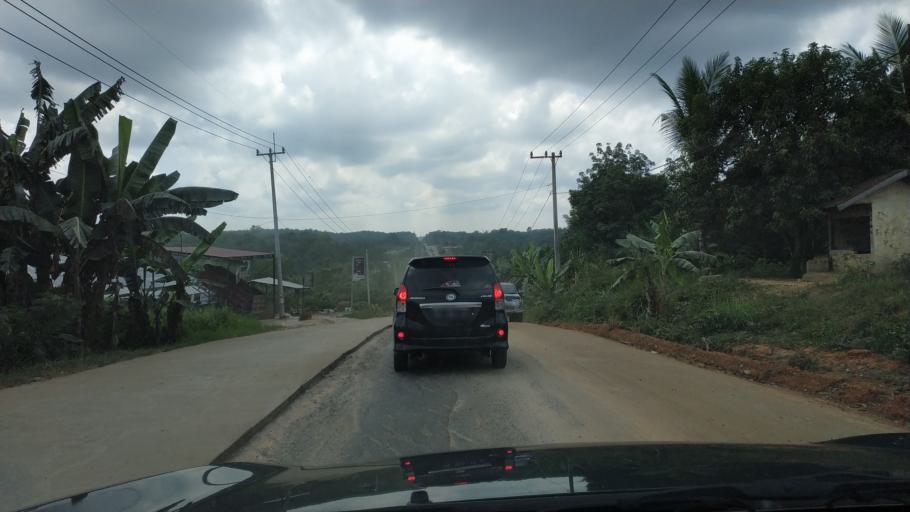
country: ID
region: Riau
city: Pangkalanbunut
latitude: 0.3054
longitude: 101.9086
